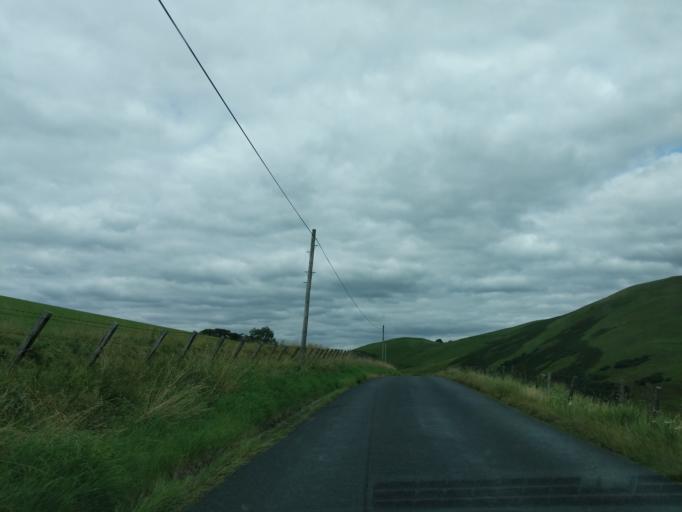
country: GB
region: Scotland
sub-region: The Scottish Borders
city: West Linton
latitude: 55.6912
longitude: -3.3335
